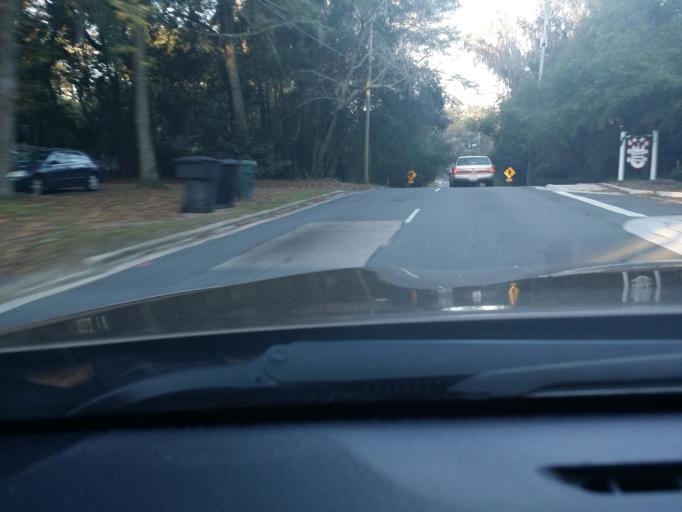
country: US
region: Florida
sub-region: Leon County
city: Tallahassee
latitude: 30.4573
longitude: -84.2706
